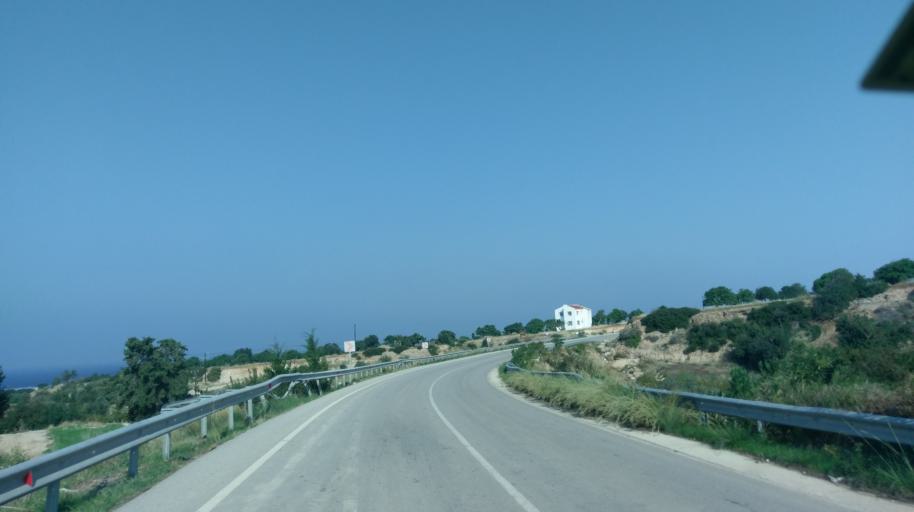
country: CY
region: Ammochostos
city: Lefkonoiko
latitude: 35.3818
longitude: 33.7201
